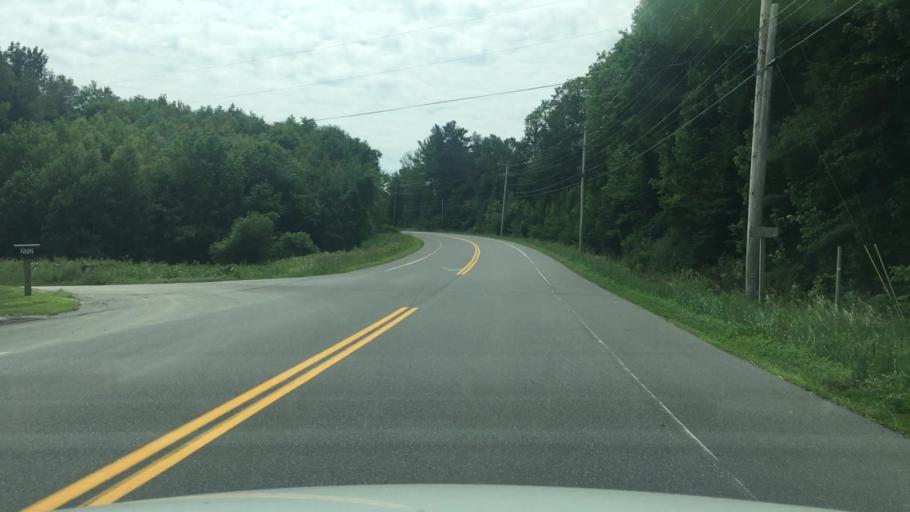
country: US
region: Maine
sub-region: Waldo County
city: Troy
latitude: 44.5693
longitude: -69.2794
